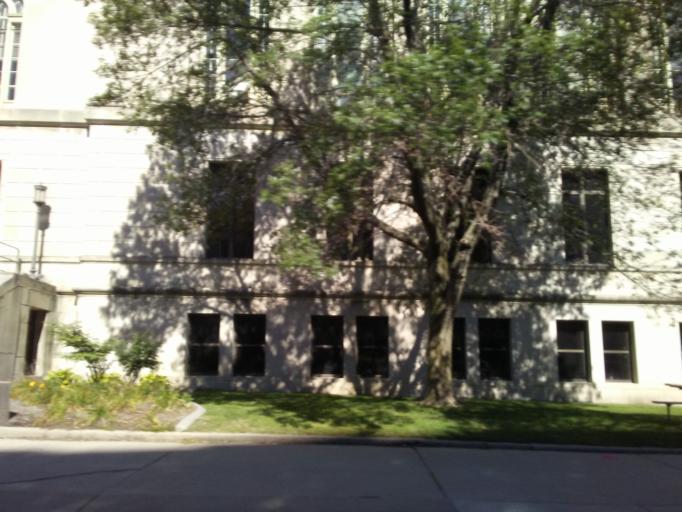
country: US
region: Wisconsin
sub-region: Dane County
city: Madison
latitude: 43.0729
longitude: -89.3809
